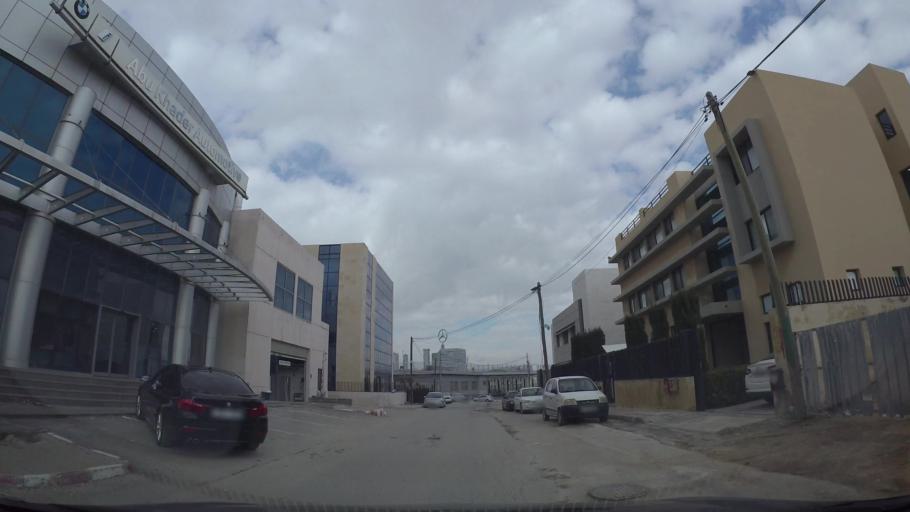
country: JO
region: Amman
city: Wadi as Sir
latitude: 31.9409
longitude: 35.8470
